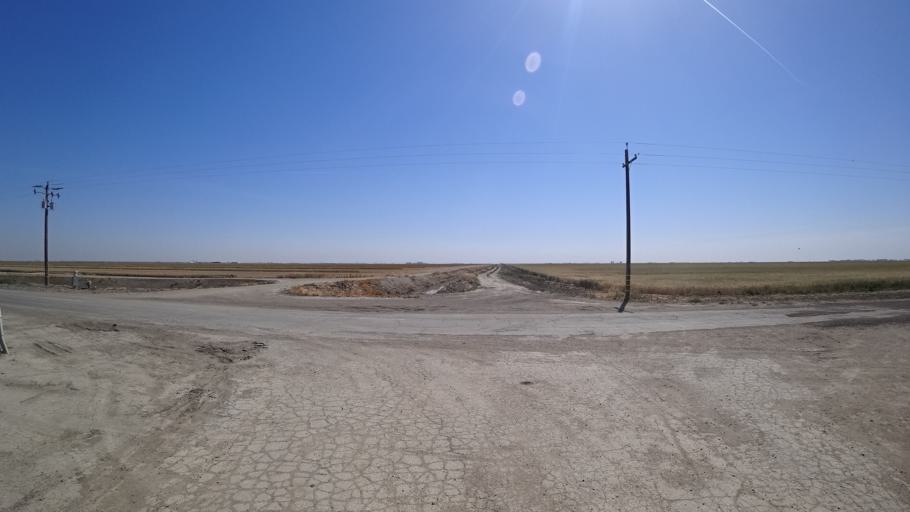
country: US
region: California
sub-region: Tulare County
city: Alpaugh
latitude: 35.9780
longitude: -119.5363
